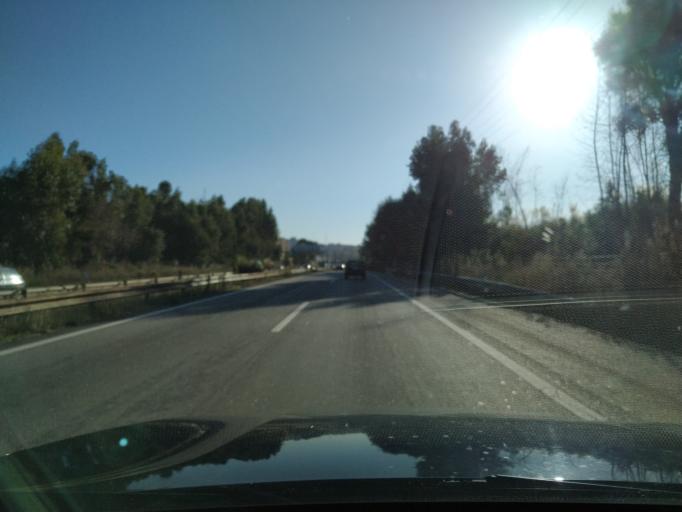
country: PT
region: Porto
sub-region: Vila Nova de Gaia
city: Vila Nova de Gaia
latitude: 41.1137
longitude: -8.6203
